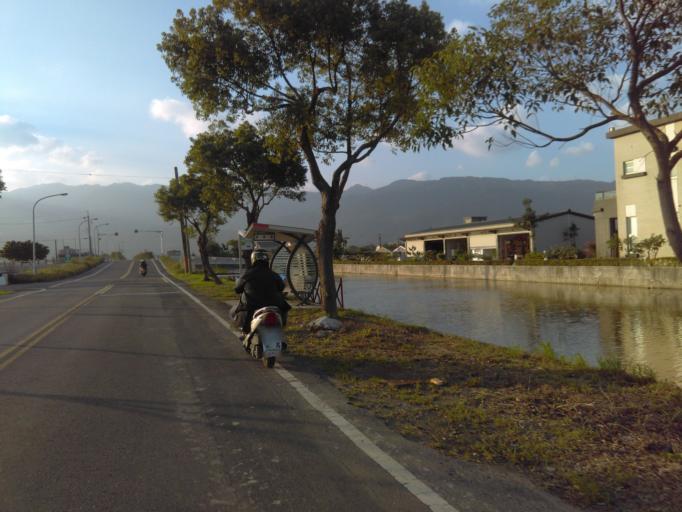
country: TW
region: Taiwan
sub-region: Yilan
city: Yilan
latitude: 24.8017
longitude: 121.7810
